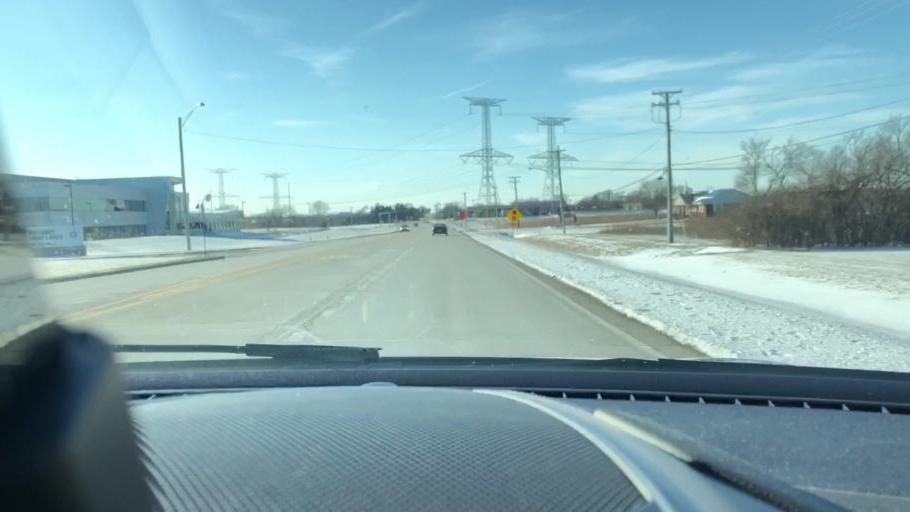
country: US
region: Illinois
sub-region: Will County
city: Ingalls Park
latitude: 41.4821
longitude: -88.0243
